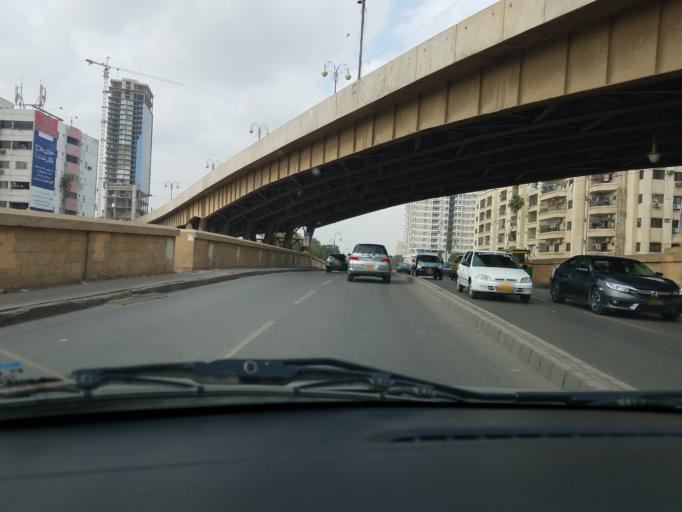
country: PK
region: Sindh
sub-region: Karachi District
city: Karachi
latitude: 24.8405
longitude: 67.0327
